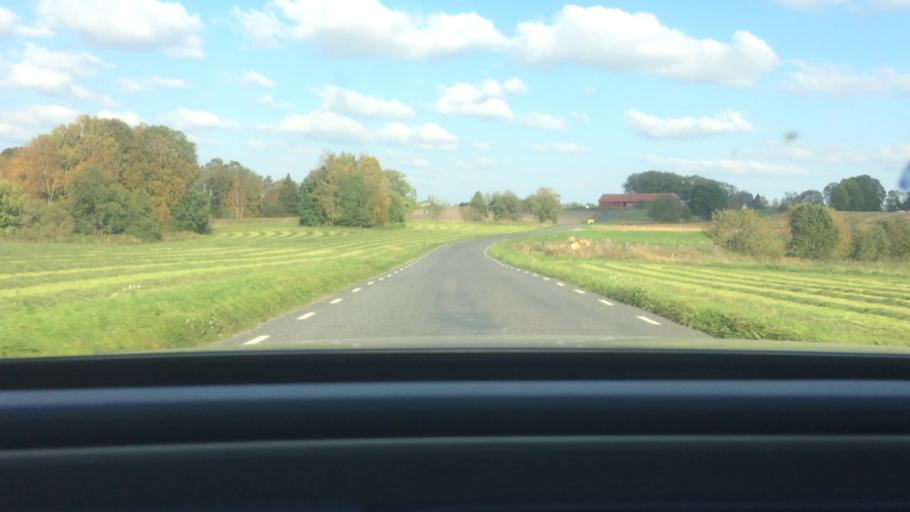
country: SE
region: Vaestra Goetaland
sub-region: Falkopings Kommun
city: Falkoeping
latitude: 58.1398
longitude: 13.5352
